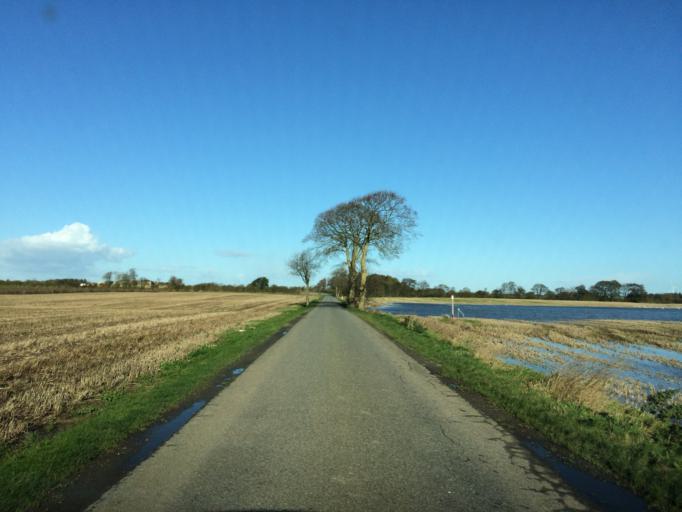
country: DK
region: South Denmark
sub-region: Fredericia Kommune
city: Taulov
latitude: 55.5560
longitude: 9.6453
